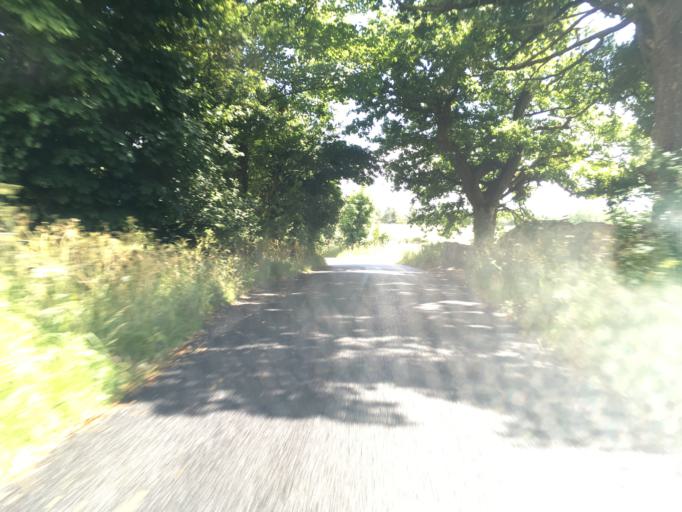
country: GB
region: England
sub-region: Gloucestershire
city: Tetbury
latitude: 51.6512
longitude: -2.1813
